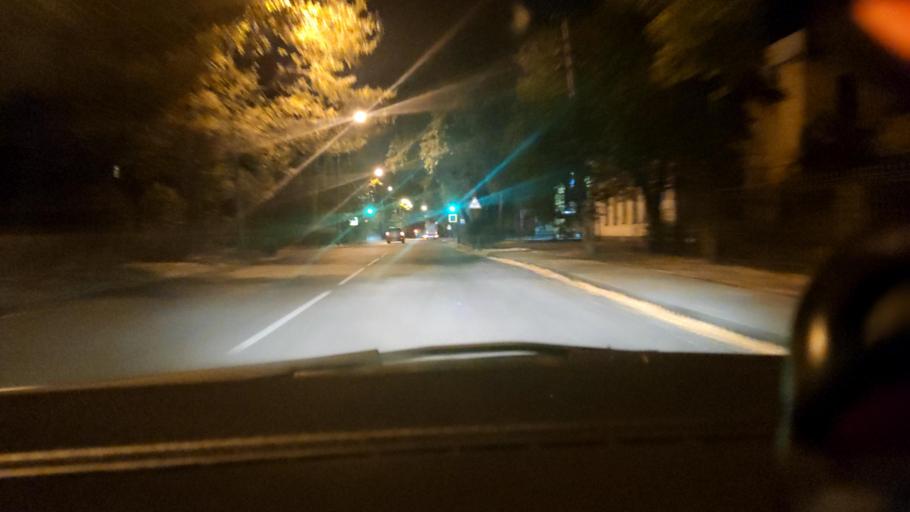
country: RU
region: Voronezj
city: Voronezh
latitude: 51.7169
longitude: 39.2217
